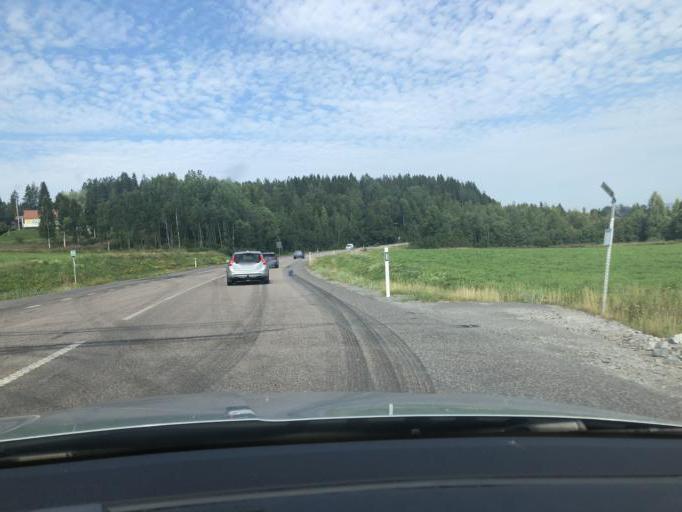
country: SE
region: Vaesternorrland
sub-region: Kramfors Kommun
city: Kramfors
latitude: 62.8816
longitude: 17.8501
